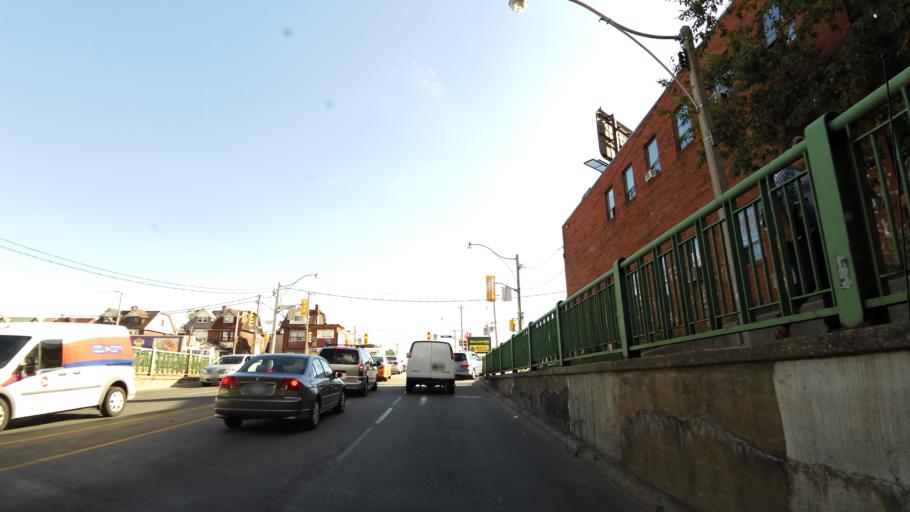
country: CA
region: Ontario
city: Toronto
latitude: 43.6689
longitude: -79.4393
